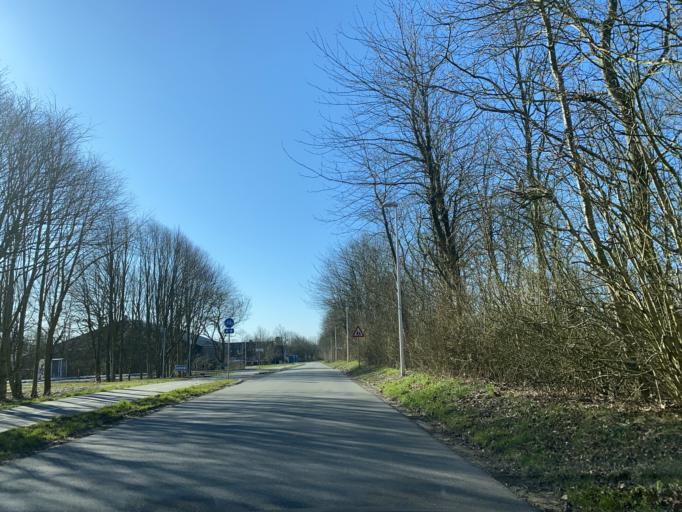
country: DK
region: Central Jutland
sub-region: Skanderborg Kommune
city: Skovby
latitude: 56.1916
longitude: 9.9635
